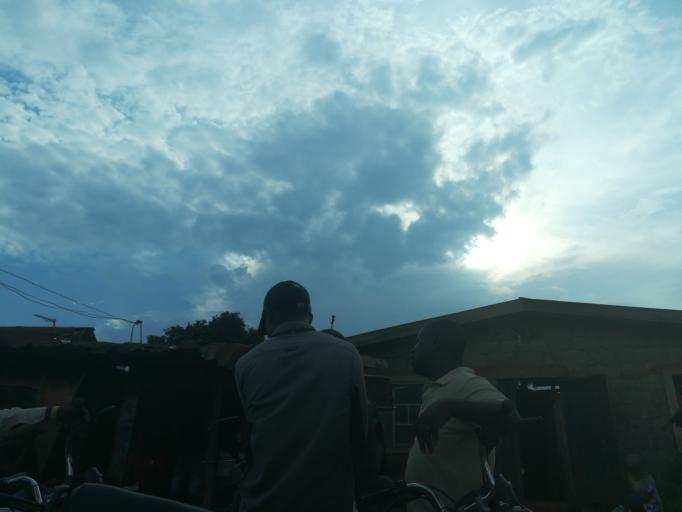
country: NG
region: Lagos
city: Ikorodu
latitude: 6.6247
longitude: 3.5012
